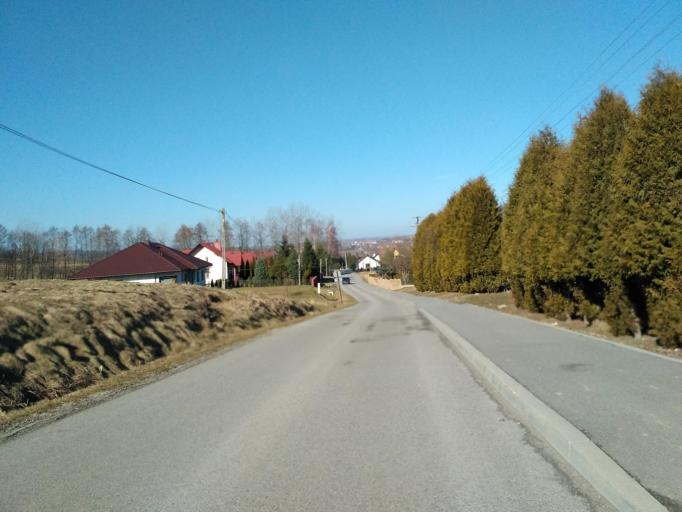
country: PL
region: Subcarpathian Voivodeship
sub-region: Powiat rzeszowski
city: Siedliska
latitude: 49.9476
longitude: 21.9532
